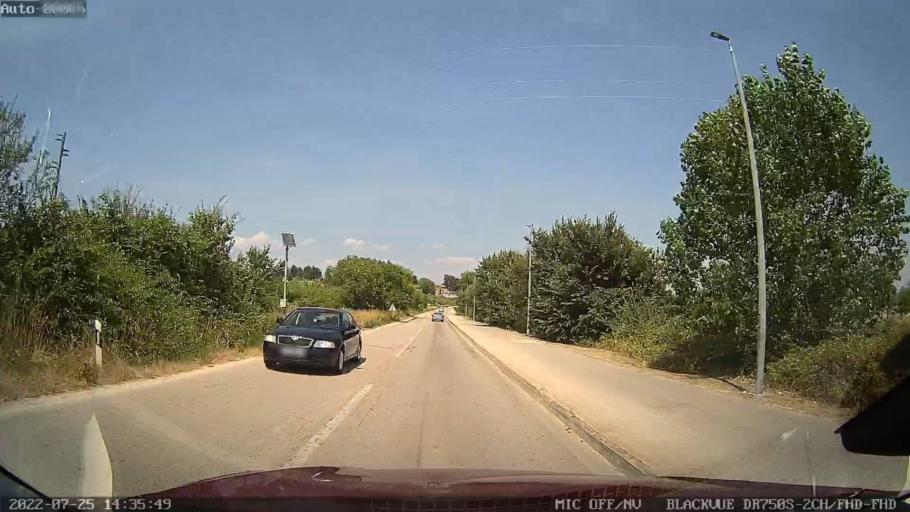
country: HR
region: Zadarska
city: Galovac
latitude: 44.1067
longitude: 15.3805
